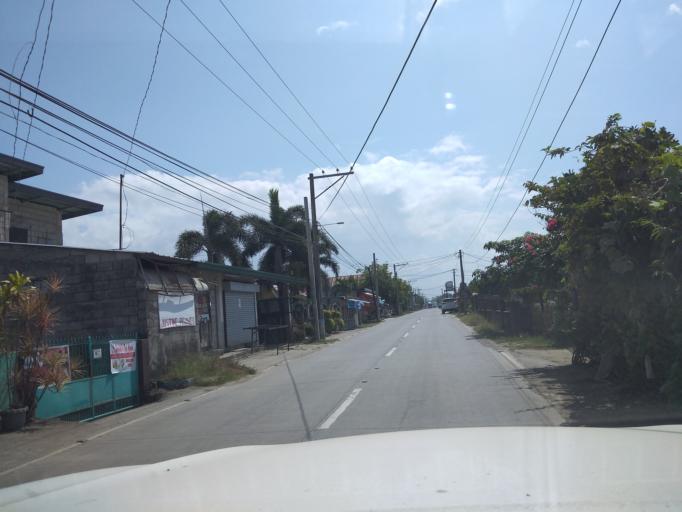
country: PH
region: Central Luzon
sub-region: Province of Pampanga
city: Talang
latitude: 15.0263
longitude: 120.8361
